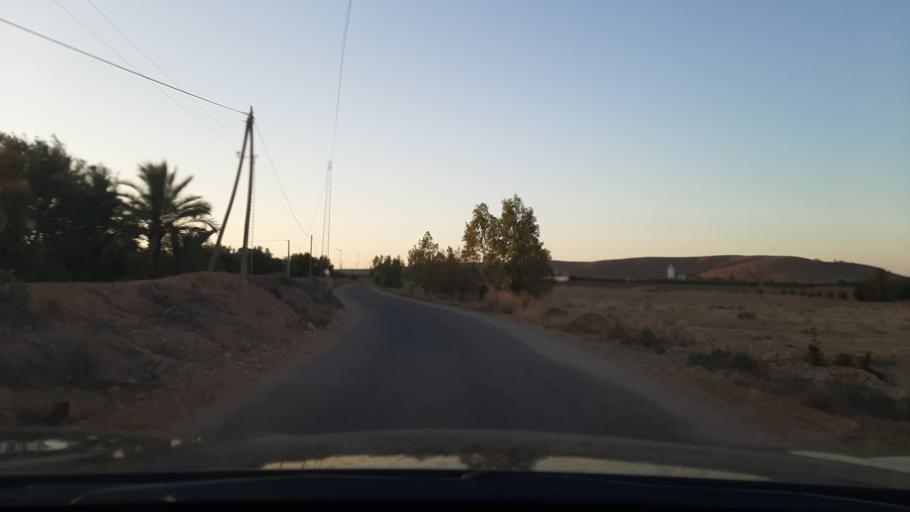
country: TN
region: Qabis
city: Matmata
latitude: 33.5648
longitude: 10.1794
